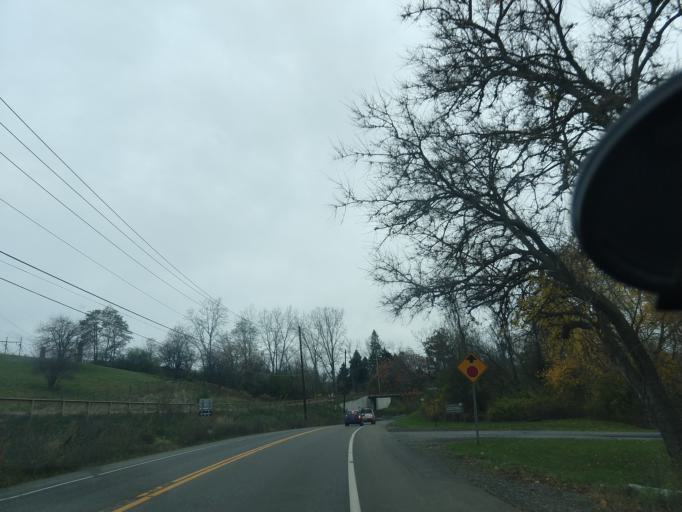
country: US
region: New York
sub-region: Tompkins County
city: East Ithaca
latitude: 42.4417
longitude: -76.4687
